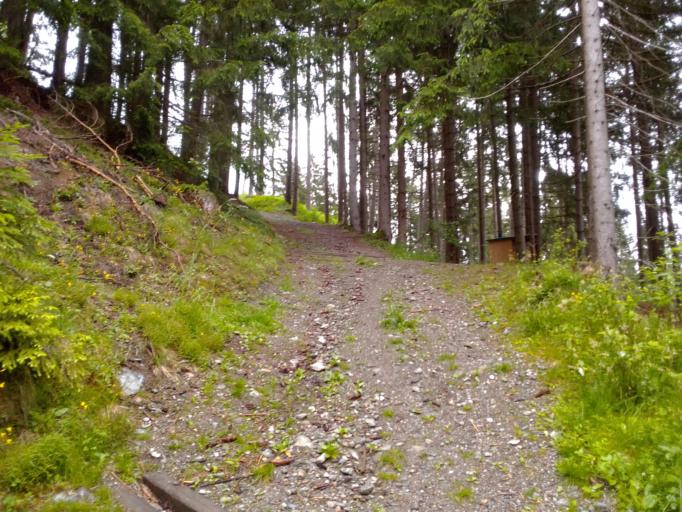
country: IT
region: Trentino-Alto Adige
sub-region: Bolzano
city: Villabassa
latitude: 46.7433
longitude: 12.1699
